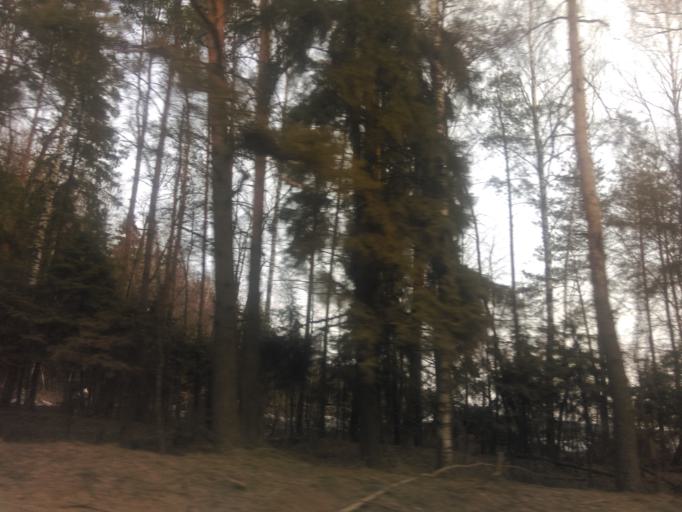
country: RU
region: Moskovskaya
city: Tuchkovo
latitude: 55.5651
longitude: 36.5285
